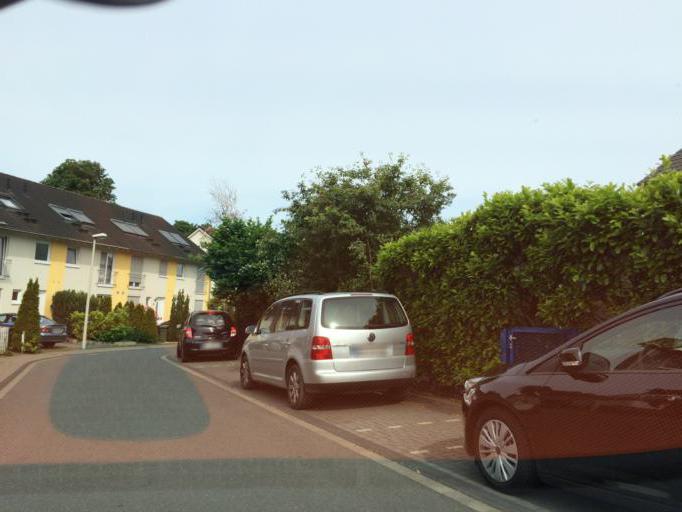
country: DE
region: North Rhine-Westphalia
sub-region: Regierungsbezirk Koln
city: Konigswinter
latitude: 50.6723
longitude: 7.1723
